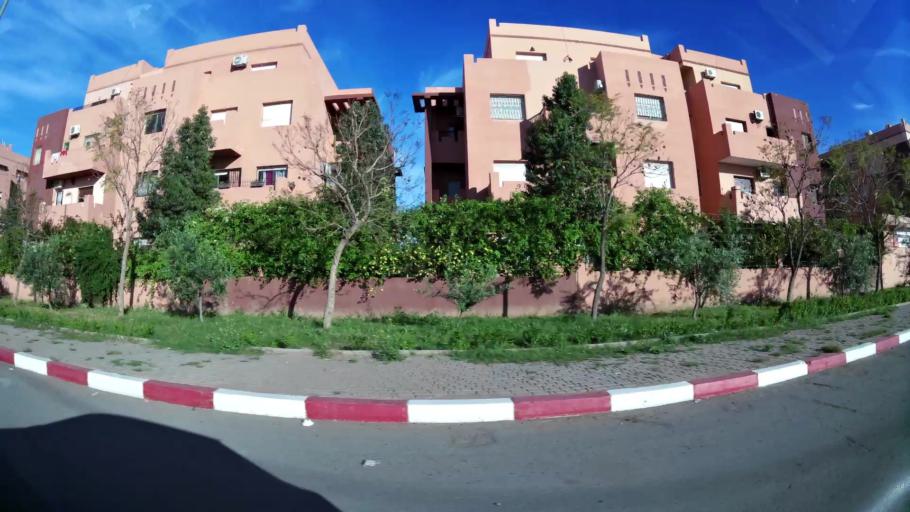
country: MA
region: Marrakech-Tensift-Al Haouz
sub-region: Marrakech
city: Marrakesh
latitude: 31.6775
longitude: -8.0663
